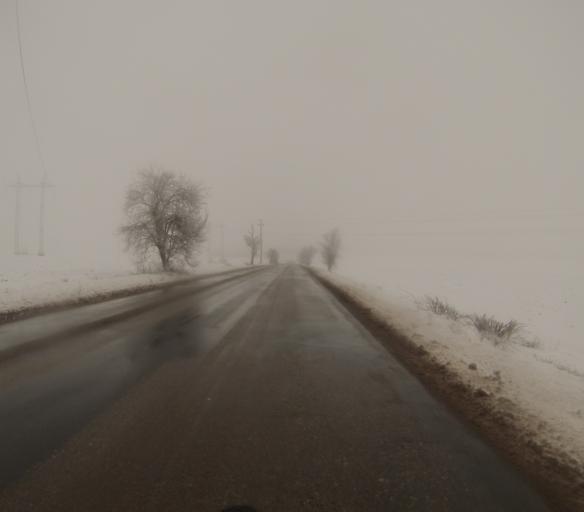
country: CZ
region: South Moravian
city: Strelice
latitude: 49.1611
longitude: 16.5054
